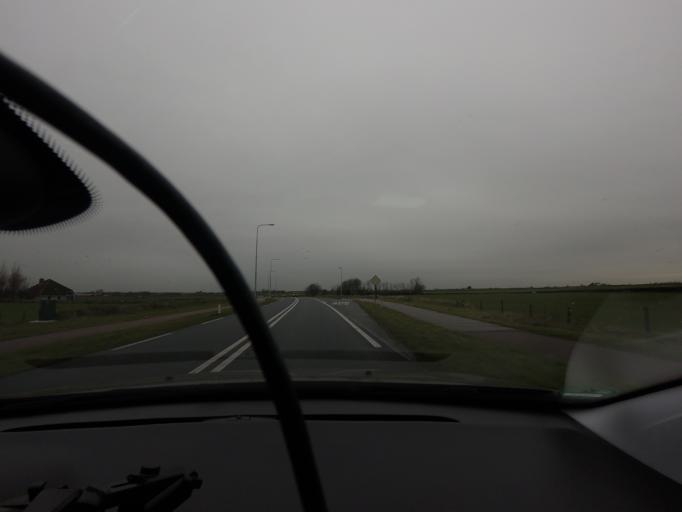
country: NL
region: North Holland
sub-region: Gemeente Texel
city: Den Burg
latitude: 53.0381
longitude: 4.8050
